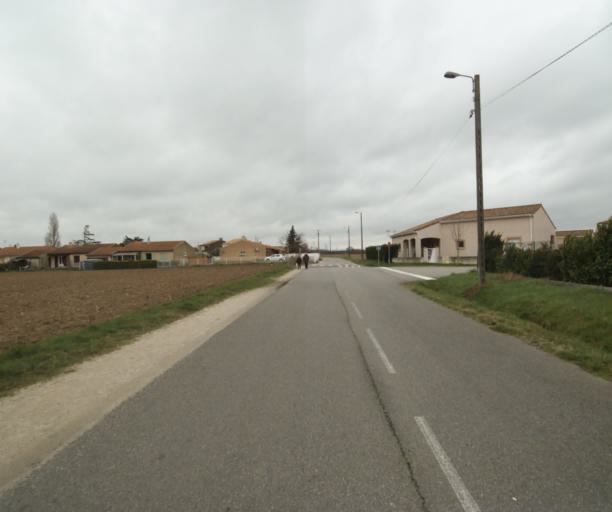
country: FR
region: Midi-Pyrenees
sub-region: Departement de l'Ariege
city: Mazeres
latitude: 43.2426
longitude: 1.6794
